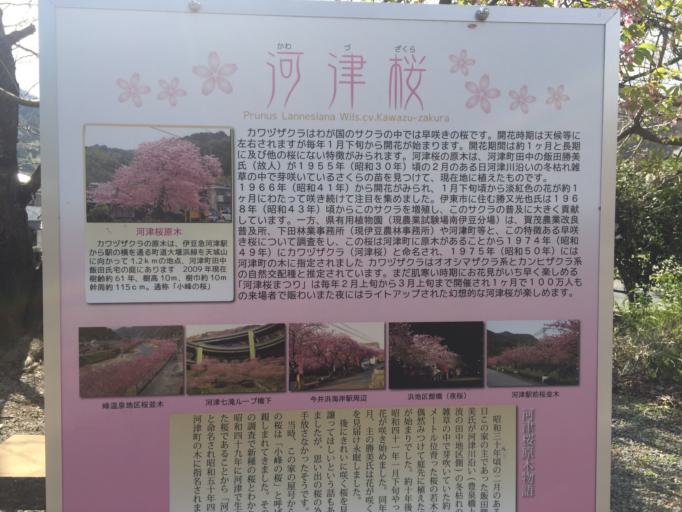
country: JP
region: Shizuoka
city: Shimoda
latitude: 34.7569
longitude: 138.9854
